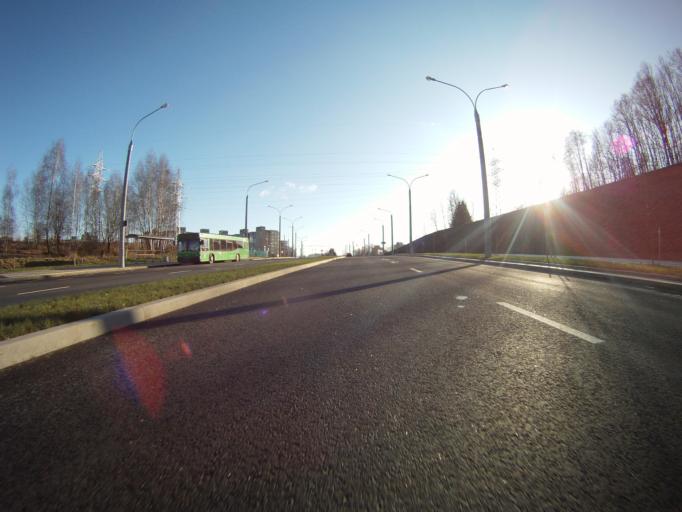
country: BY
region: Minsk
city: Novoye Medvezhino
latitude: 53.8715
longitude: 27.4580
